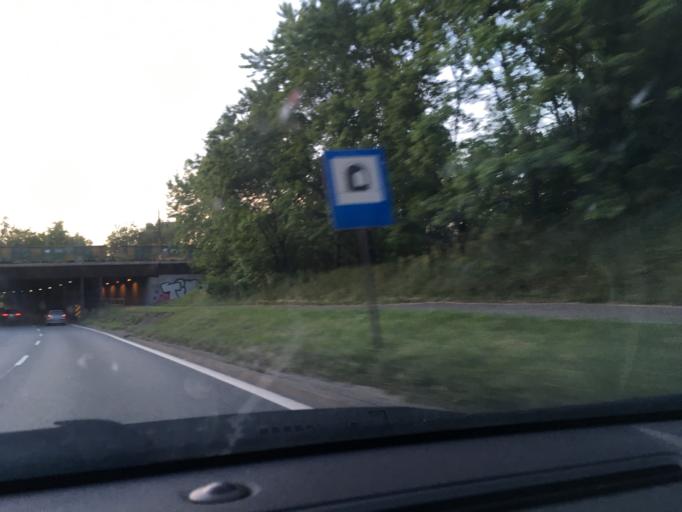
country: PL
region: Silesian Voivodeship
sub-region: Katowice
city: Katowice
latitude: 50.2564
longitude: 19.0484
